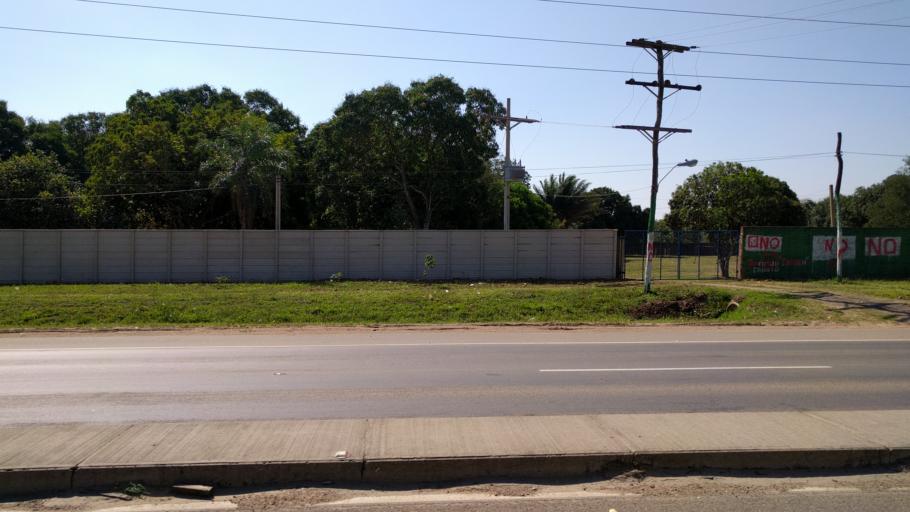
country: BO
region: Santa Cruz
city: Cotoca
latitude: -17.7642
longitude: -63.0335
